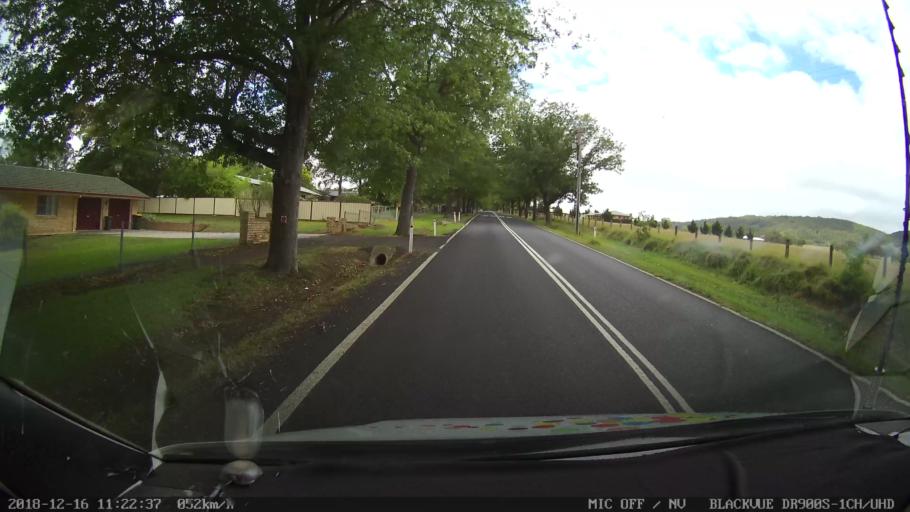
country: AU
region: New South Wales
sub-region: Tenterfield Municipality
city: Carrolls Creek
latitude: -29.0530
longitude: 152.0282
